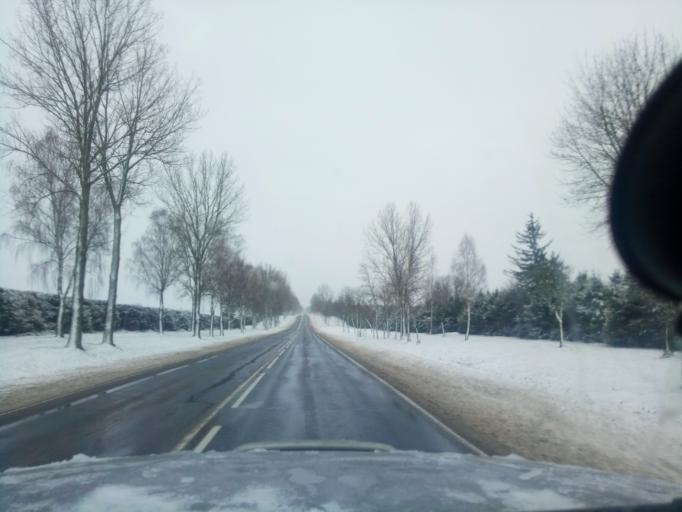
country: BY
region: Minsk
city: Haradzyeya
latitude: 53.3535
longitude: 26.5163
